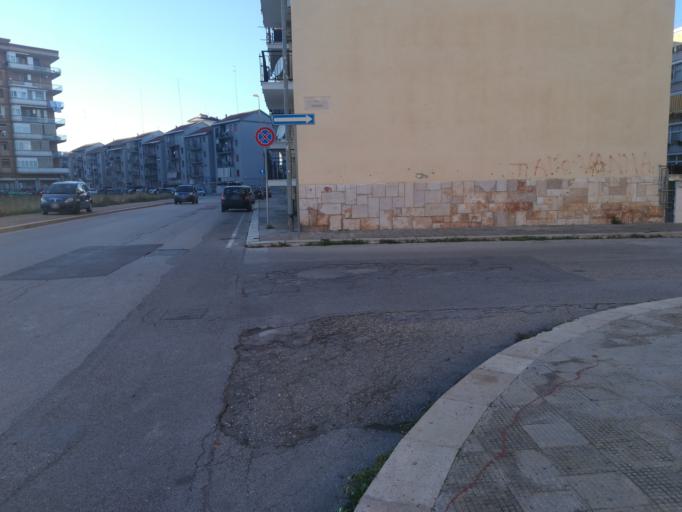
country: IT
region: Apulia
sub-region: Provincia di Bari
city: San Paolo
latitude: 41.1179
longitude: 16.7918
